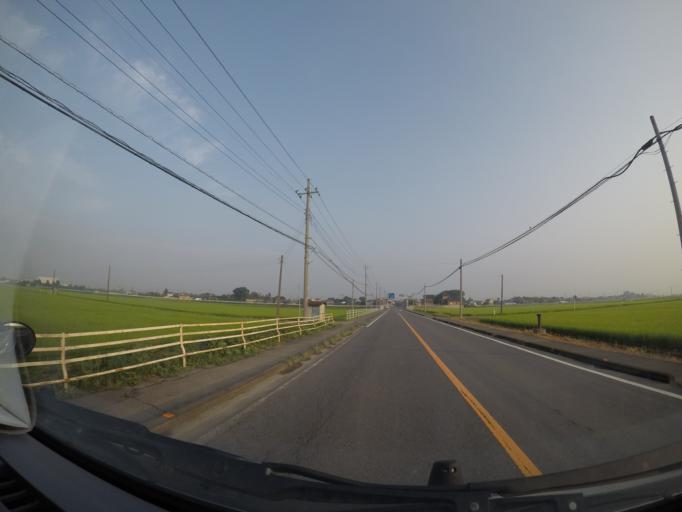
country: JP
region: Tochigi
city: Fujioka
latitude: 36.2774
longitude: 139.7103
